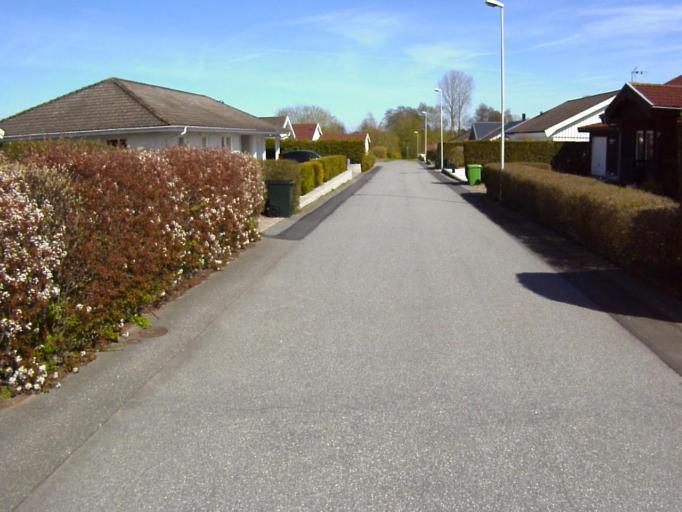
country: SE
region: Skane
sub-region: Kristianstads Kommun
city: Onnestad
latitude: 55.9985
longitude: 14.0692
